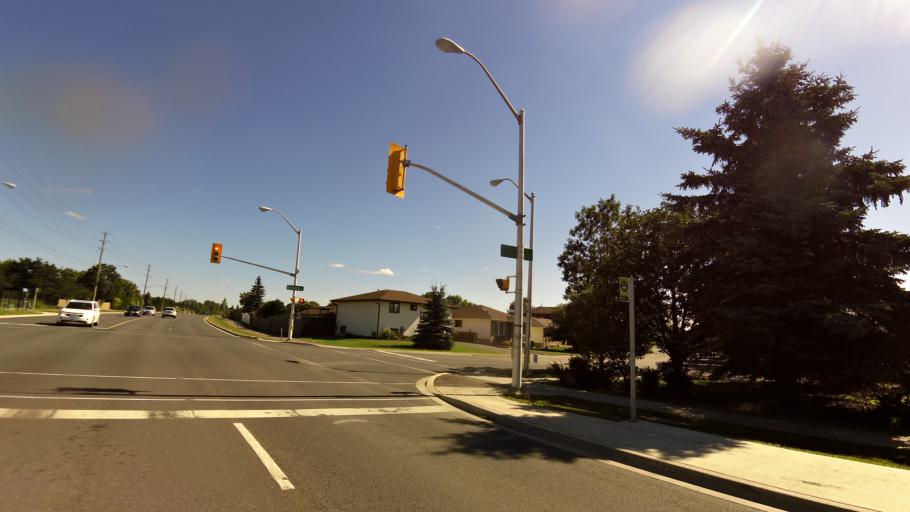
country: CA
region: Ontario
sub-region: Thunder Bay District
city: Thunder Bay
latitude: 48.4331
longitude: -89.2727
